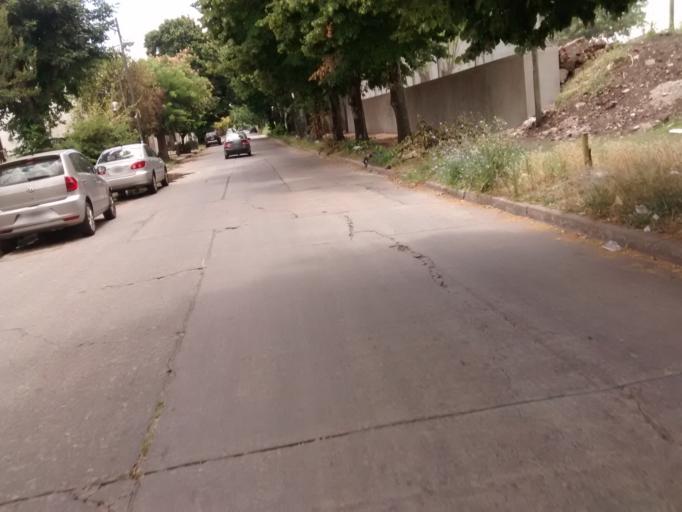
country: AR
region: Buenos Aires
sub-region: Partido de La Plata
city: La Plata
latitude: -34.9442
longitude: -57.9444
